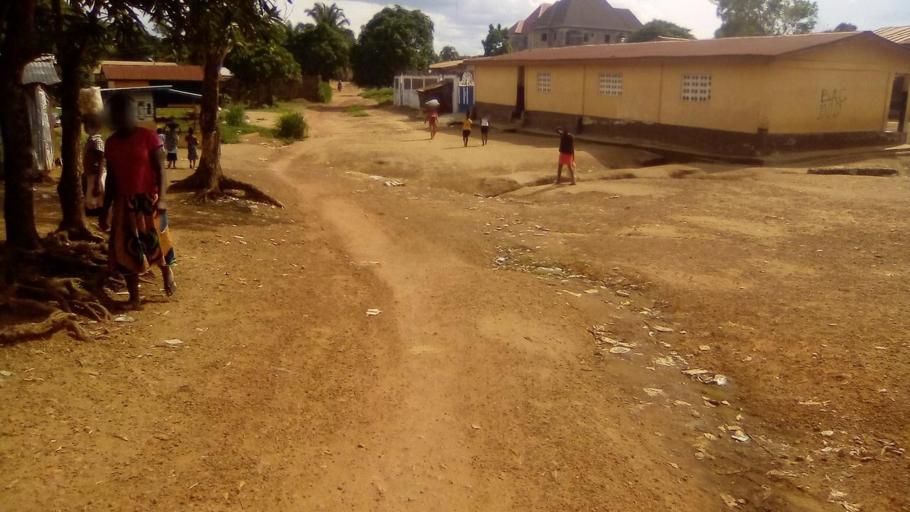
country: SL
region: Southern Province
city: Bo
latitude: 7.9512
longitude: -11.7214
